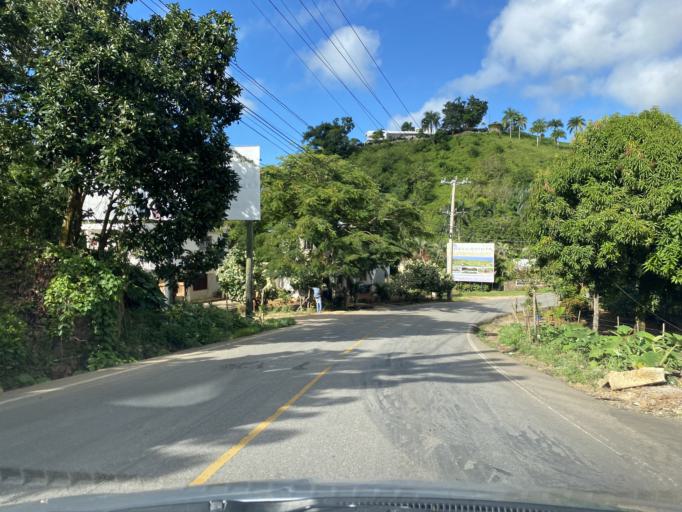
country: DO
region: Samana
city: Las Terrenas
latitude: 19.2820
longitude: -69.5545
